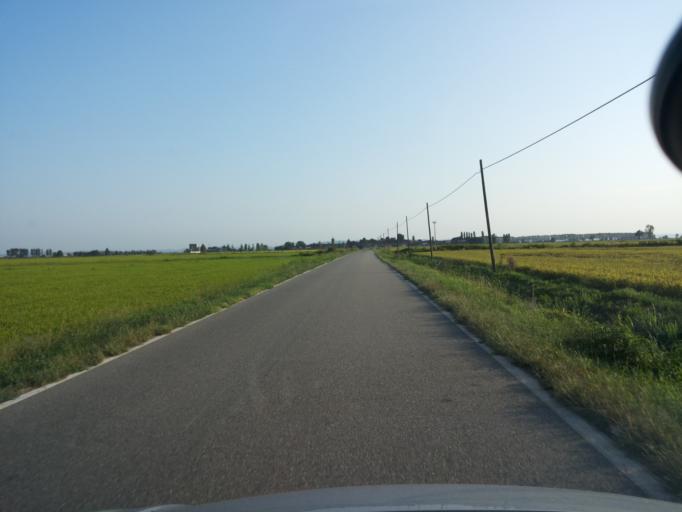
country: IT
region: Piedmont
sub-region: Provincia di Vercelli
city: Sali Vercellese
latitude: 45.3195
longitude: 8.3333
